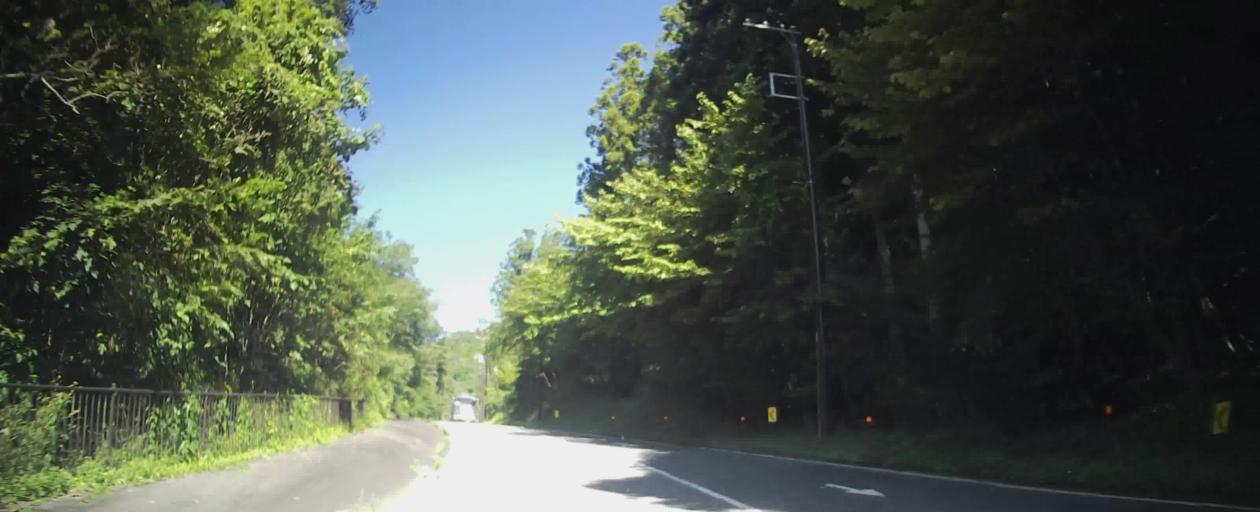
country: JP
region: Gunma
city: Nakanojomachi
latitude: 36.5622
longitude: 138.7261
